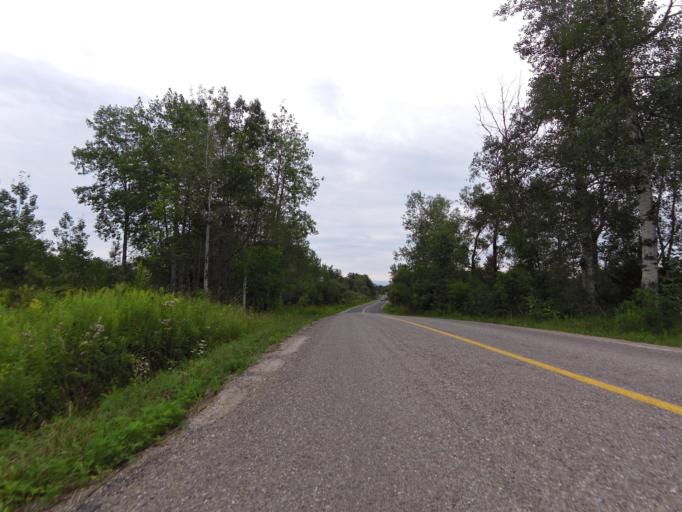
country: CA
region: Ontario
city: Kingston
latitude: 44.6182
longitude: -76.6461
